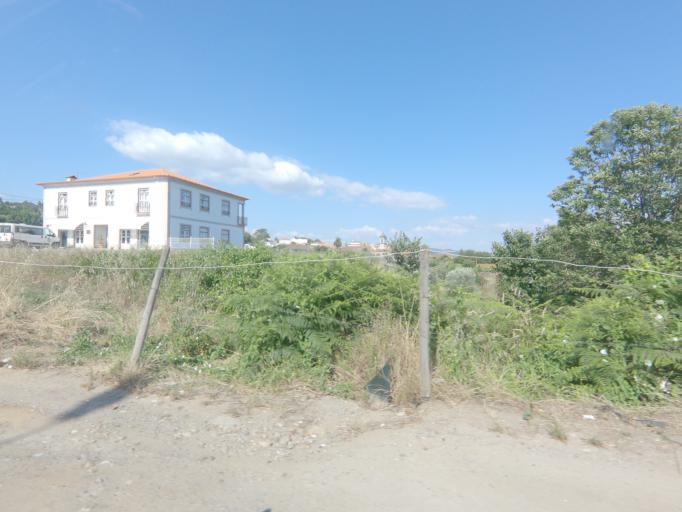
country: PT
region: Vila Real
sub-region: Sabrosa
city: Sabrosa
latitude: 41.2644
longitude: -7.5787
